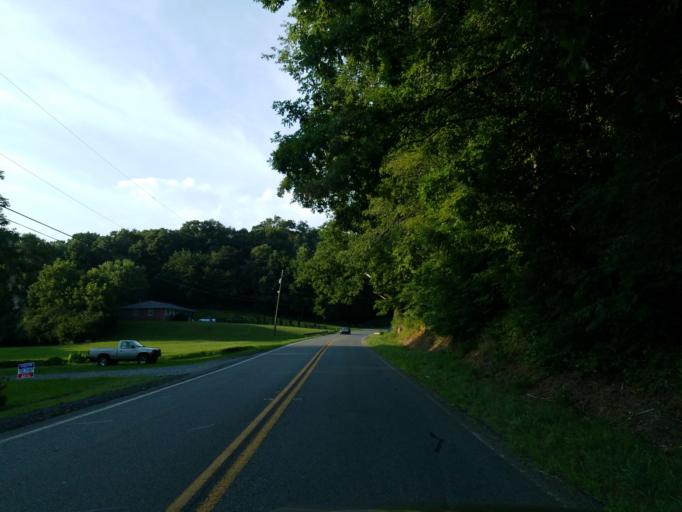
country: US
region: Georgia
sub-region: Gilmer County
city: Ellijay
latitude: 34.6267
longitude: -84.5160
